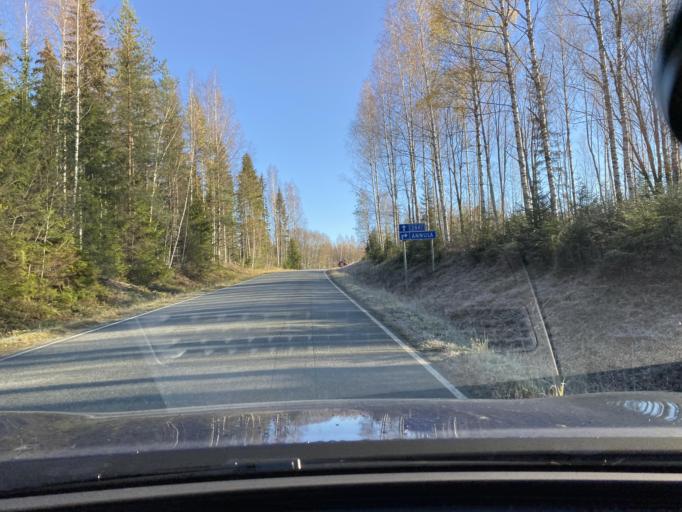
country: FI
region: Pirkanmaa
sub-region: Etelae-Pirkanmaa
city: Kylmaekoski
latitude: 61.0555
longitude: 23.7103
